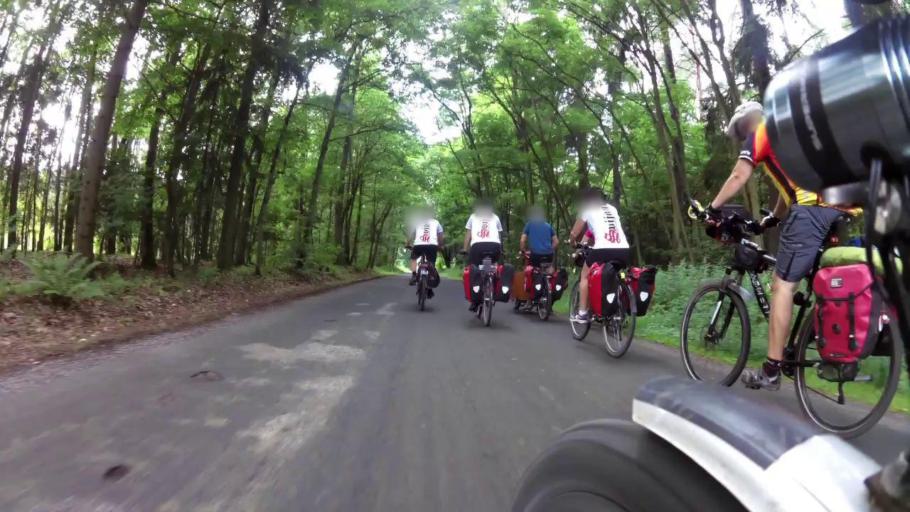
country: PL
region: West Pomeranian Voivodeship
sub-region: Powiat mysliborski
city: Debno
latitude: 52.7887
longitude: 14.6723
